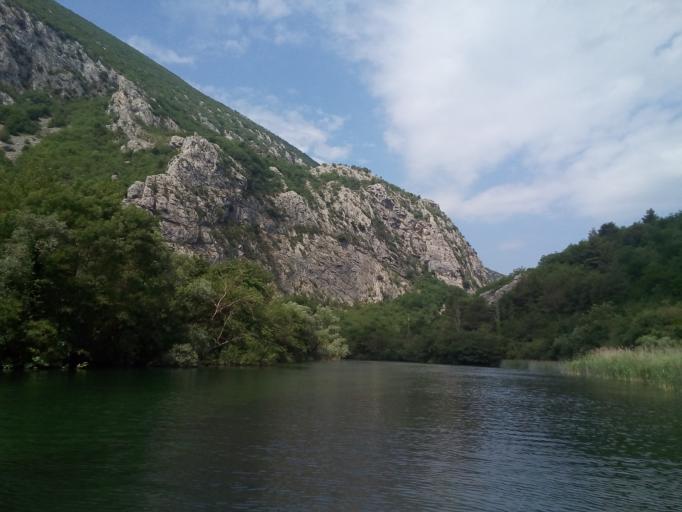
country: HR
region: Splitsko-Dalmatinska
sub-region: Grad Omis
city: Omis
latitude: 43.4410
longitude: 16.7418
